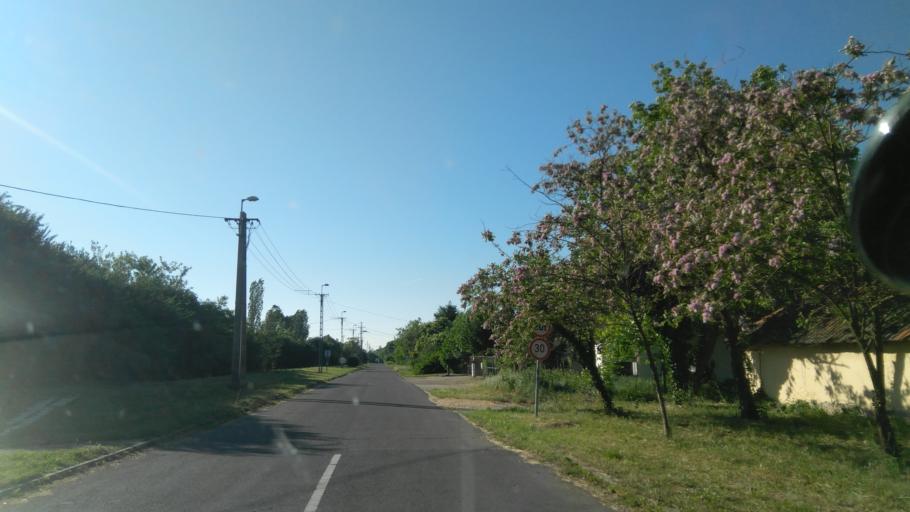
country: HU
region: Bekes
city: Gyula
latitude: 46.6388
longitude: 21.2549
